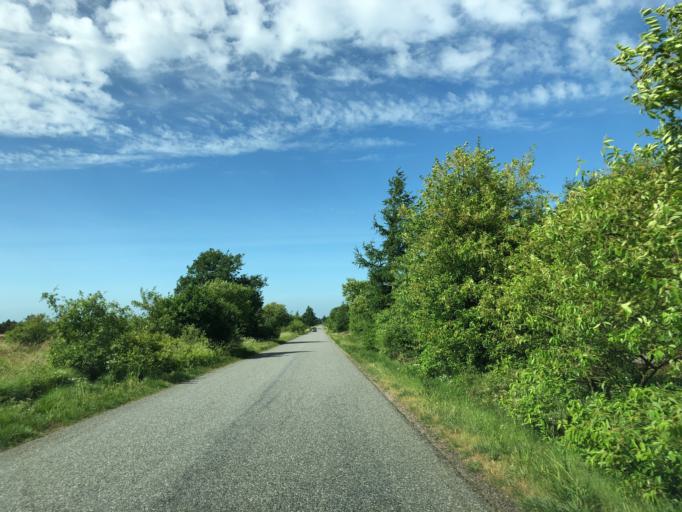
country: DK
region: Central Jutland
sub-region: Herning Kommune
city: Kibaek
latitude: 56.0675
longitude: 8.9158
